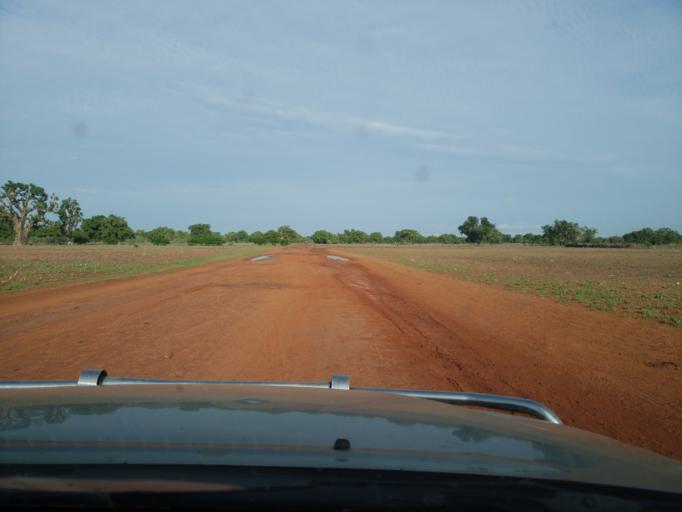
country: ML
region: Sikasso
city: Koutiala
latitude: 12.4205
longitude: -5.6945
